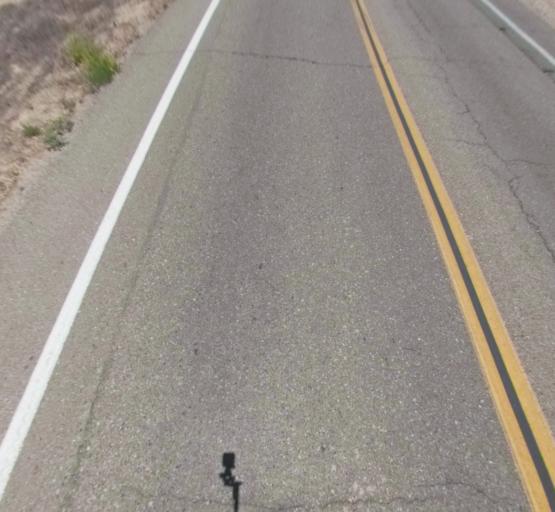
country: US
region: California
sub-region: Madera County
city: Chowchilla
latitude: 37.1143
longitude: -120.3222
